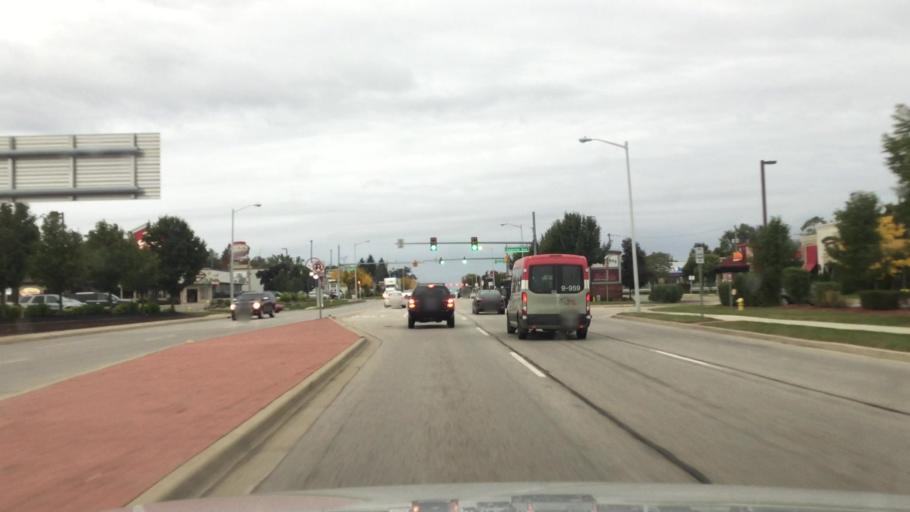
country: US
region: Michigan
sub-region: Kalamazoo County
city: Portage
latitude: 42.2352
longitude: -85.5896
